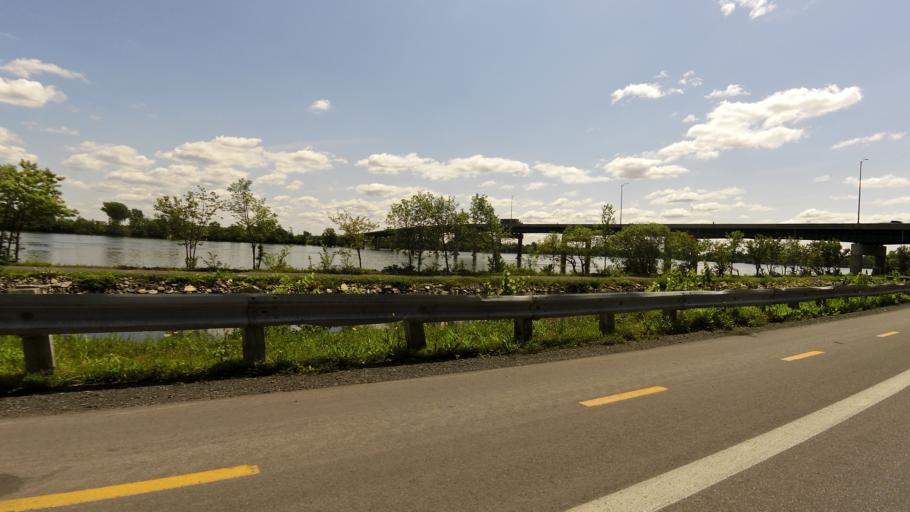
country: CA
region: Quebec
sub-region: Monteregie
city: Saint-Jean-sur-Richelieu
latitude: 45.3280
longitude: -73.2636
